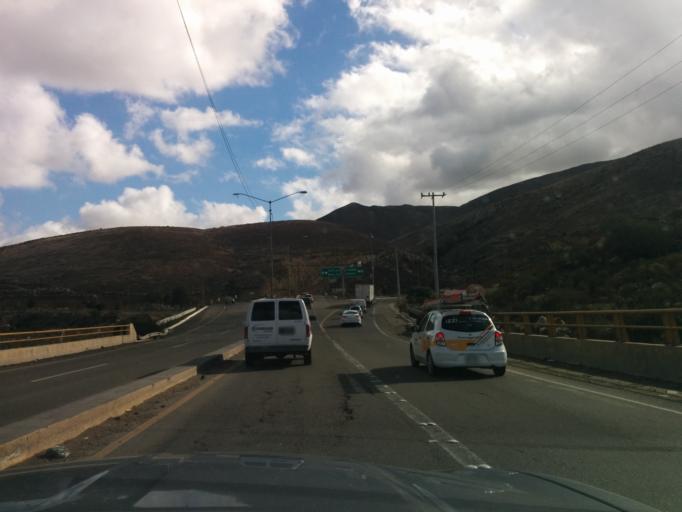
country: MX
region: Baja California
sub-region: Tijuana
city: Ejido Javier Rojo Gomez
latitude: 32.5423
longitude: -116.8574
